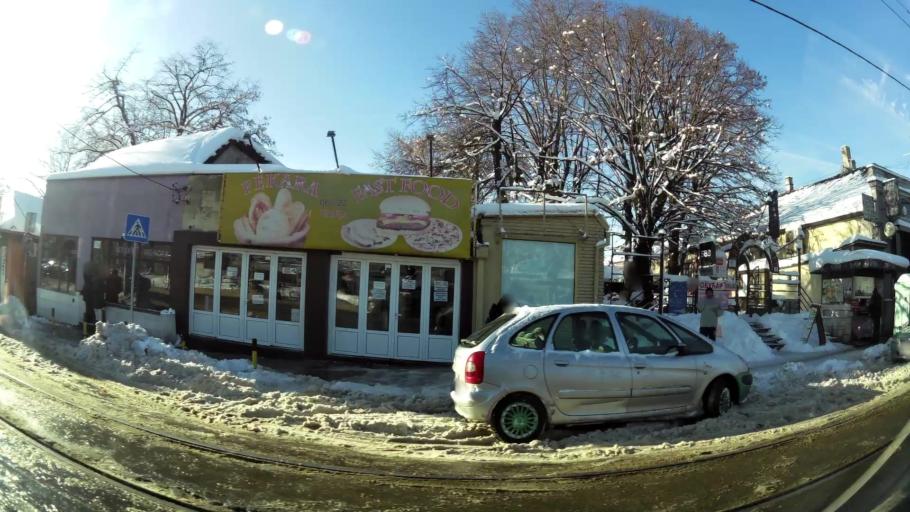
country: RS
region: Central Serbia
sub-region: Belgrade
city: Palilula
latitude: 44.7929
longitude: 20.5052
